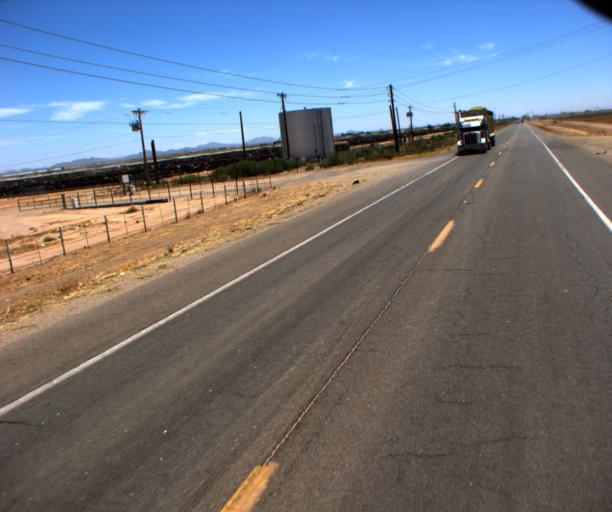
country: US
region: Arizona
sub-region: Pinal County
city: Maricopa
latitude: 32.8793
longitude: -112.0156
